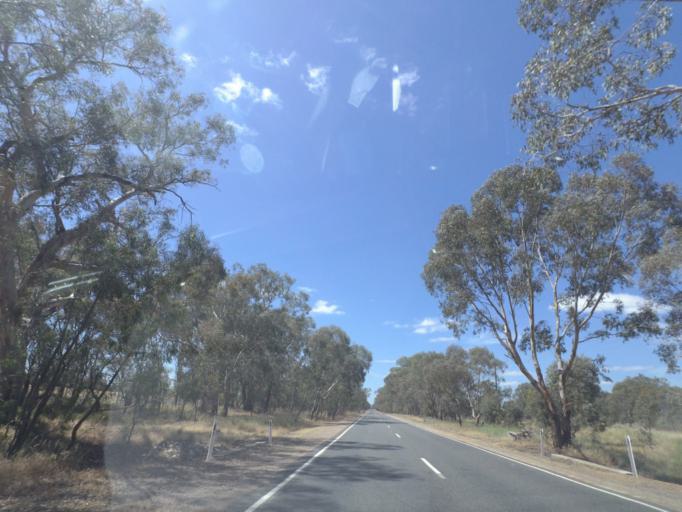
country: AU
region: Victoria
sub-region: Wangaratta
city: Wangaratta
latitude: -36.4338
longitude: 146.2512
